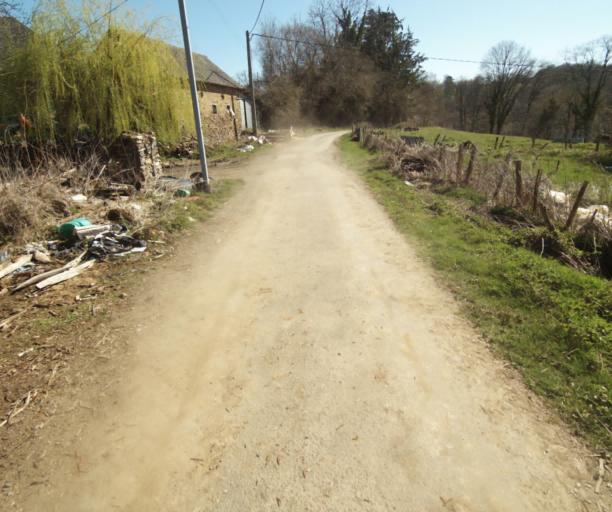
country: FR
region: Limousin
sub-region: Departement de la Correze
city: Uzerche
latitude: 45.4096
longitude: 1.6338
